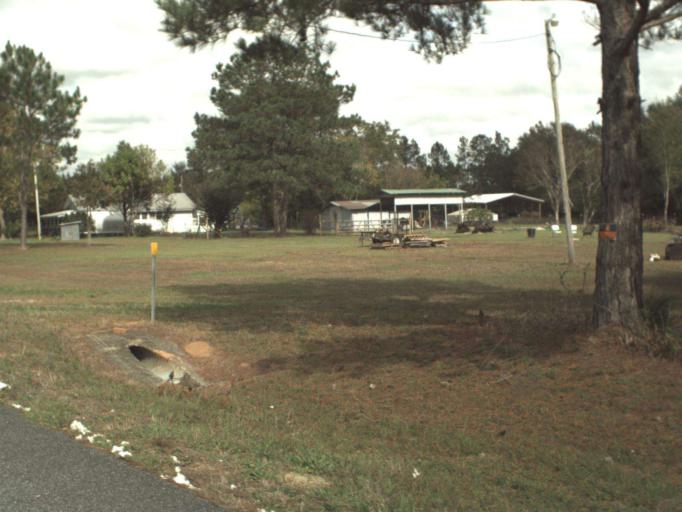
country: US
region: Florida
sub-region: Santa Rosa County
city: Wallace
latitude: 30.8125
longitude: -87.1305
